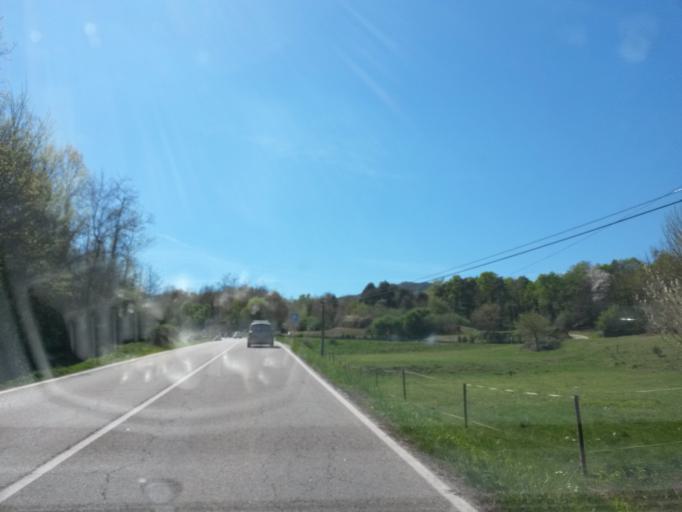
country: ES
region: Catalonia
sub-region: Provincia de Girona
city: Sant Cristofol de les Fonts
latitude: 42.1565
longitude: 2.5154
